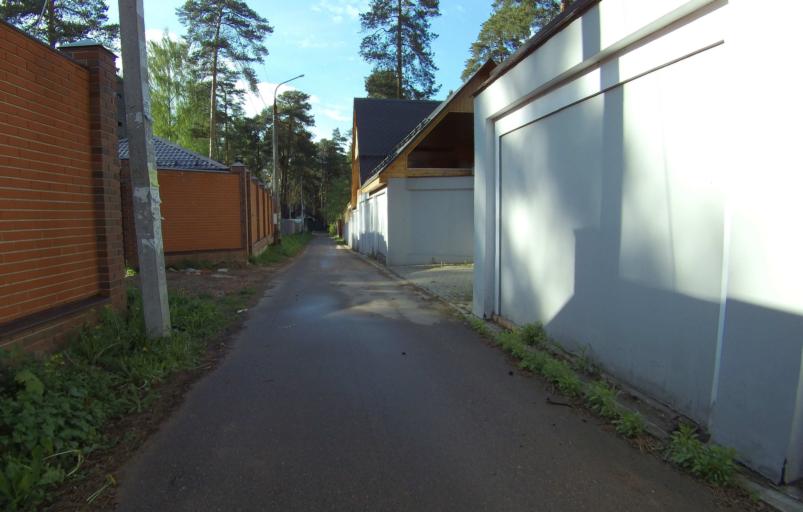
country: RU
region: Moskovskaya
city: Kratovo
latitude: 55.5933
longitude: 38.1660
